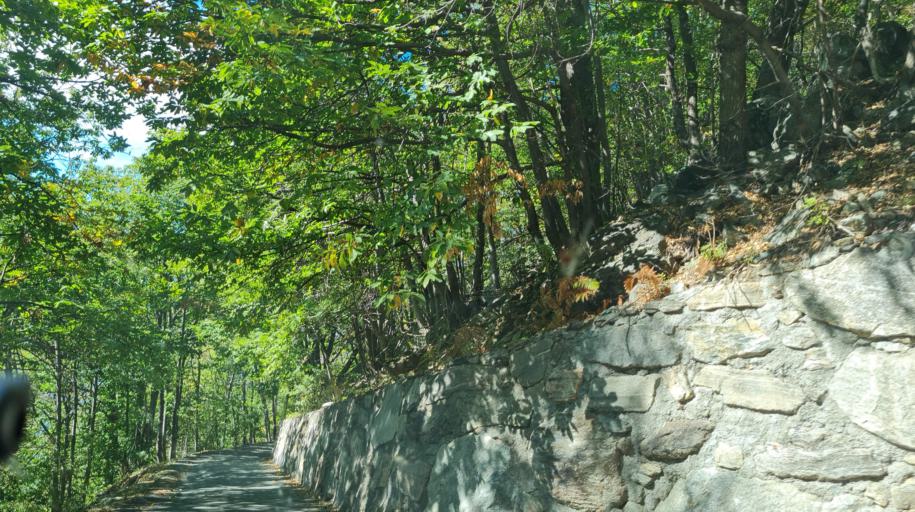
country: IT
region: Aosta Valley
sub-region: Valle d'Aosta
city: Arnad
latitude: 45.6434
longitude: 7.7468
